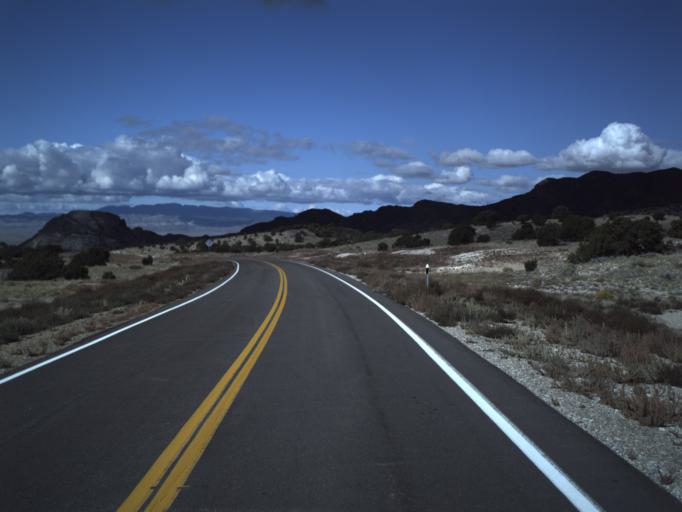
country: US
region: Utah
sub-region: Beaver County
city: Milford
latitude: 38.5175
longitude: -113.5473
